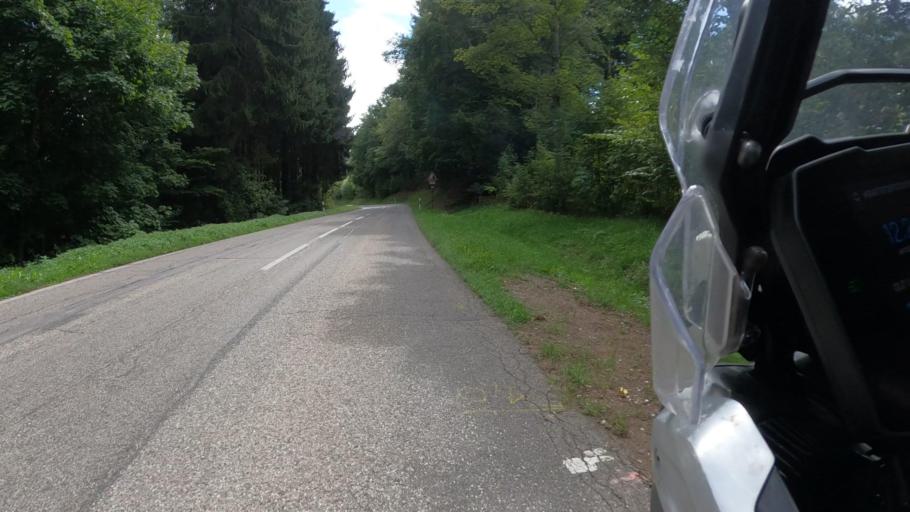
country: DE
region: Baden-Wuerttemberg
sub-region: Freiburg Region
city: Weilheim
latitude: 47.6867
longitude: 8.2557
